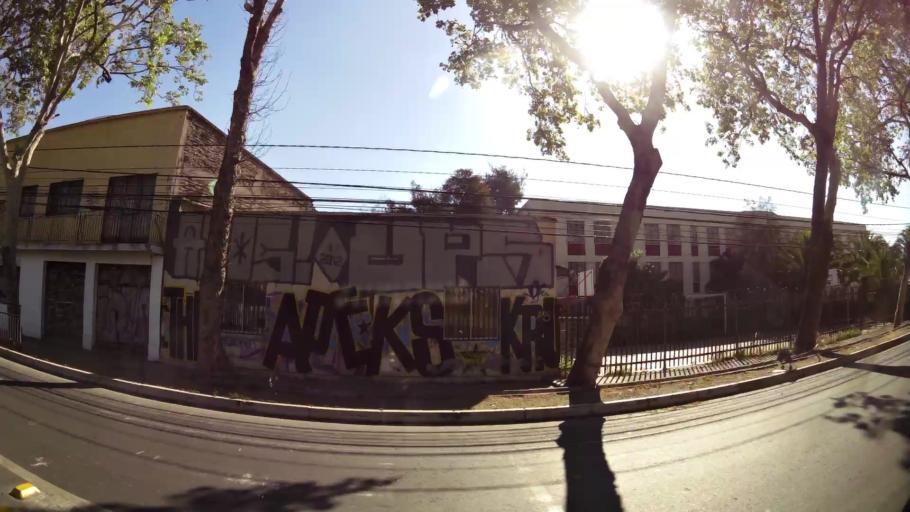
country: CL
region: Santiago Metropolitan
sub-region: Provincia de Maipo
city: San Bernardo
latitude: -33.6078
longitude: -70.6972
